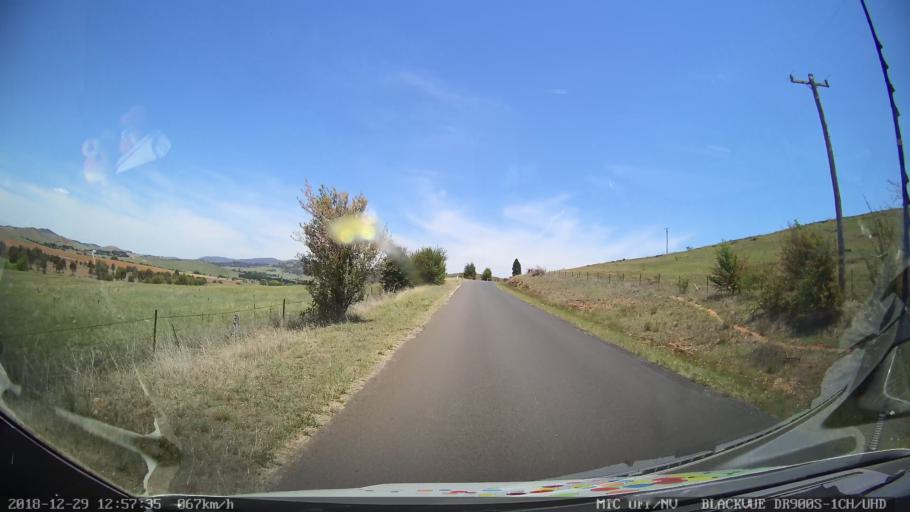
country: AU
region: Australian Capital Territory
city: Macarthur
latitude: -35.7091
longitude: 149.1760
